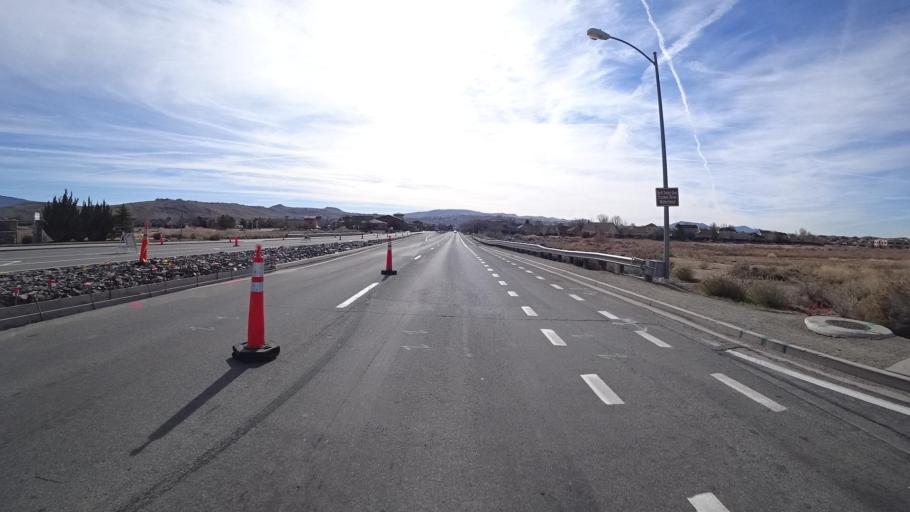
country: US
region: Nevada
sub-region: Washoe County
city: Sun Valley
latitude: 39.5904
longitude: -119.7298
